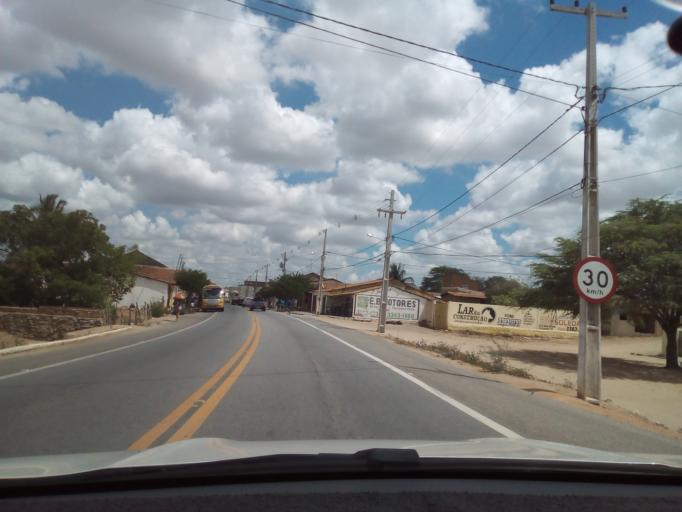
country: BR
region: Paraiba
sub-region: Soledade
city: Soledade
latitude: -7.0585
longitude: -36.3575
